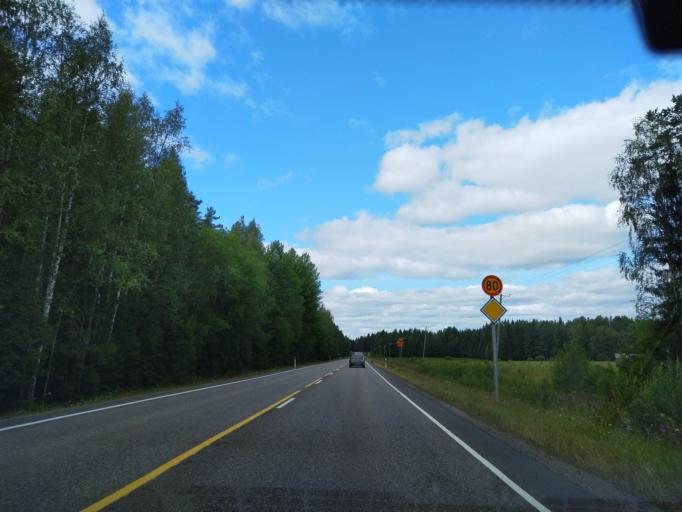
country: FI
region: Haeme
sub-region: Haemeenlinna
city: Renko
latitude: 60.7546
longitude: 24.3030
